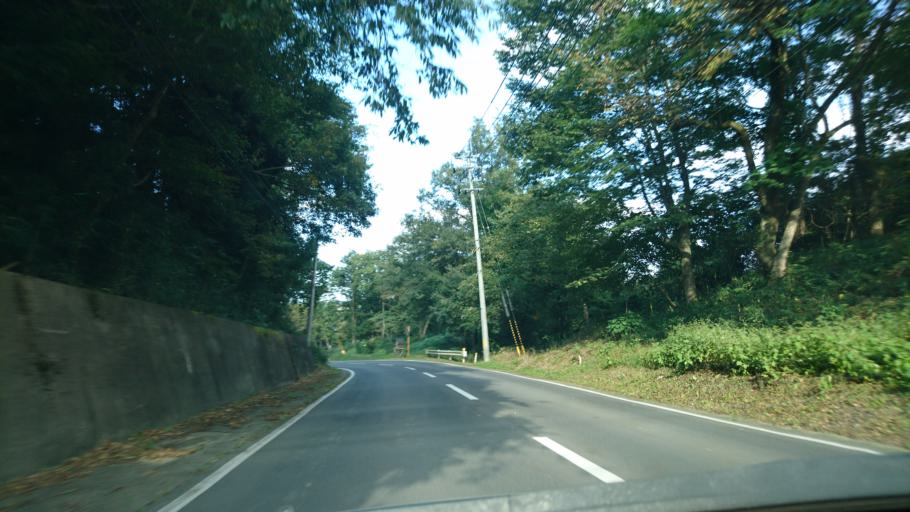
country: JP
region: Iwate
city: Ichinoseki
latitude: 38.8318
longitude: 141.2247
